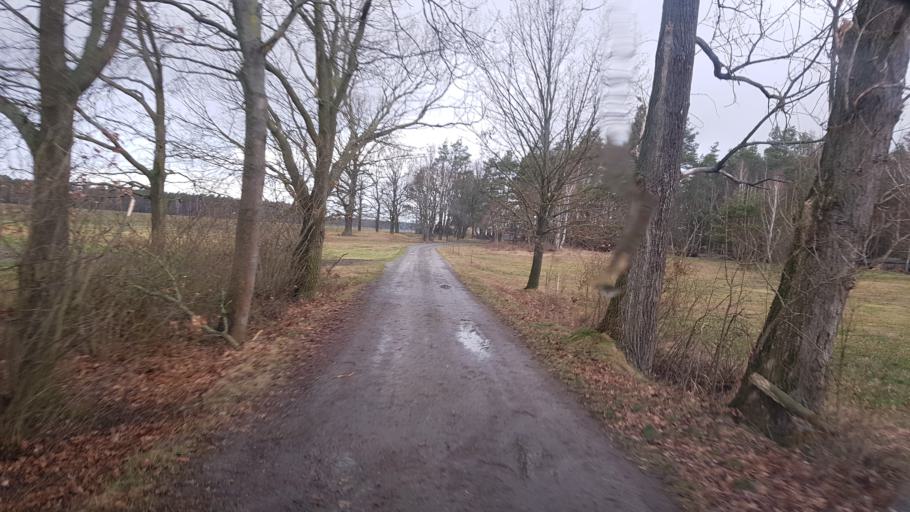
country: DE
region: Brandenburg
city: Sallgast
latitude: 51.6093
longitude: 13.8403
